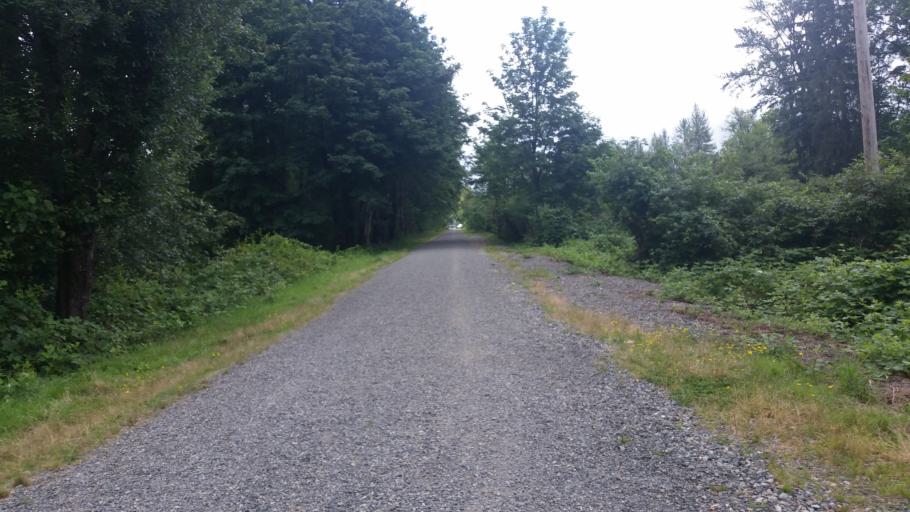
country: US
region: Washington
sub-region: King County
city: Snoqualmie
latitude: 47.5224
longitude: -121.8014
